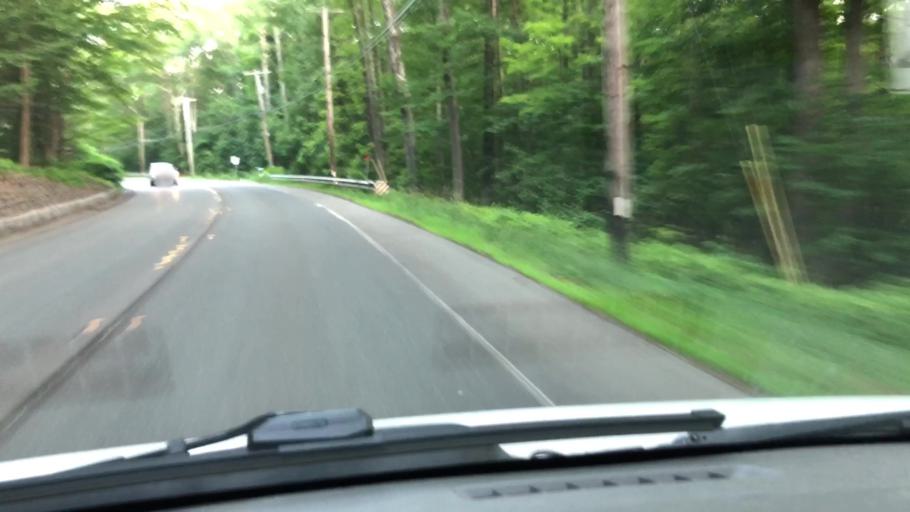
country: US
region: Massachusetts
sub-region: Hampshire County
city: Williamsburg
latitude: 42.4163
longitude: -72.7637
